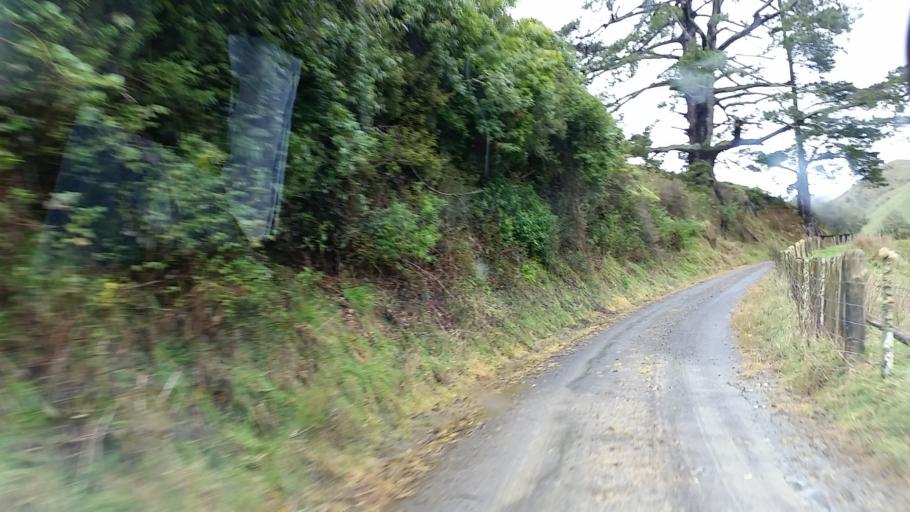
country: NZ
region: Taranaki
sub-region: South Taranaki District
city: Eltham
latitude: -39.4868
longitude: 174.4348
